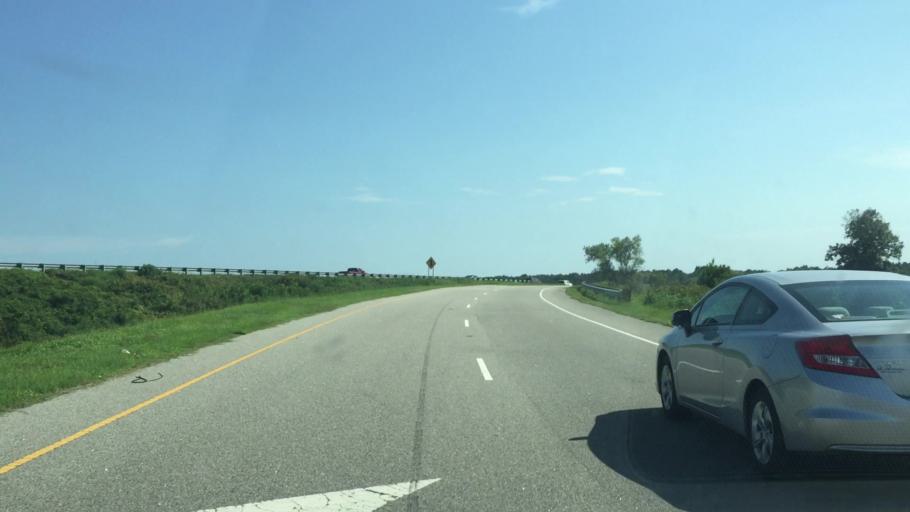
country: US
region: South Carolina
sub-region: Horry County
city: North Myrtle Beach
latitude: 33.8437
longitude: -78.7025
